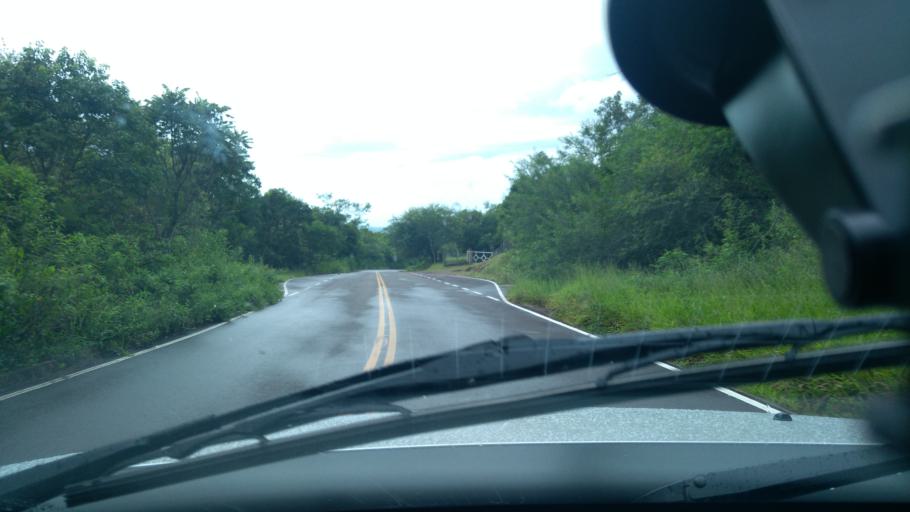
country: BR
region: Rio Grande do Sul
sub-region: Torres
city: Torres
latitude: -29.1961
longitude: -49.9763
